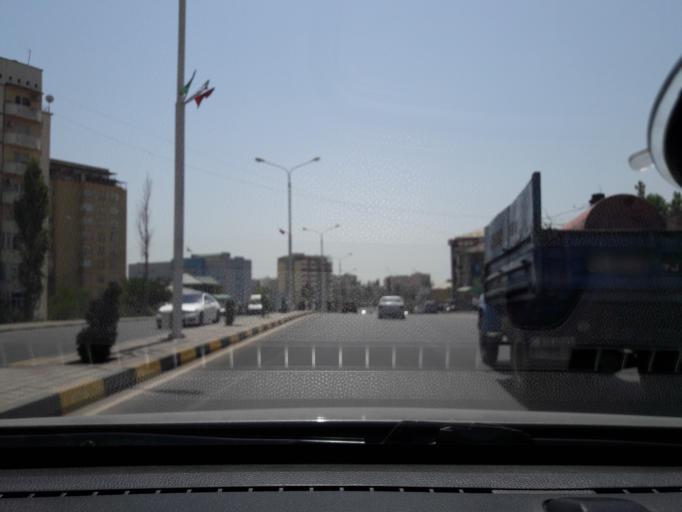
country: TJ
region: Dushanbe
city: Dushanbe
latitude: 38.5875
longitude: 68.7157
